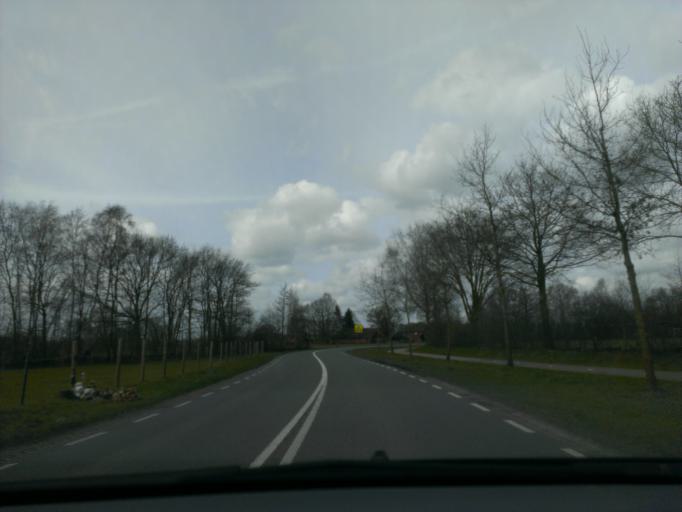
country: NL
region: Overijssel
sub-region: Gemeente Borne
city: Borne
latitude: 52.2972
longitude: 6.7304
